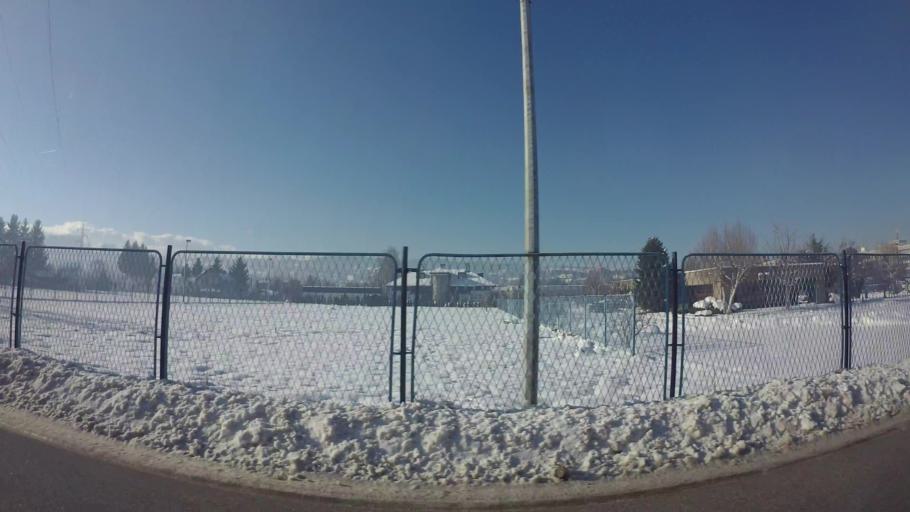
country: BA
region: Federation of Bosnia and Herzegovina
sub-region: Kanton Sarajevo
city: Sarajevo
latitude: 43.8224
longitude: 18.3777
